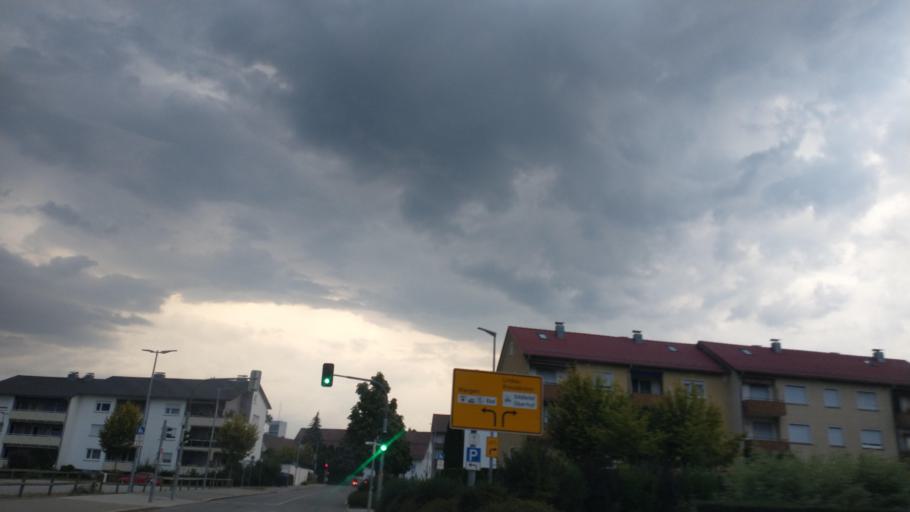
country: DE
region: Baden-Wuerttemberg
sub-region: Tuebingen Region
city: Tettnang
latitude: 47.6682
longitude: 9.5892
